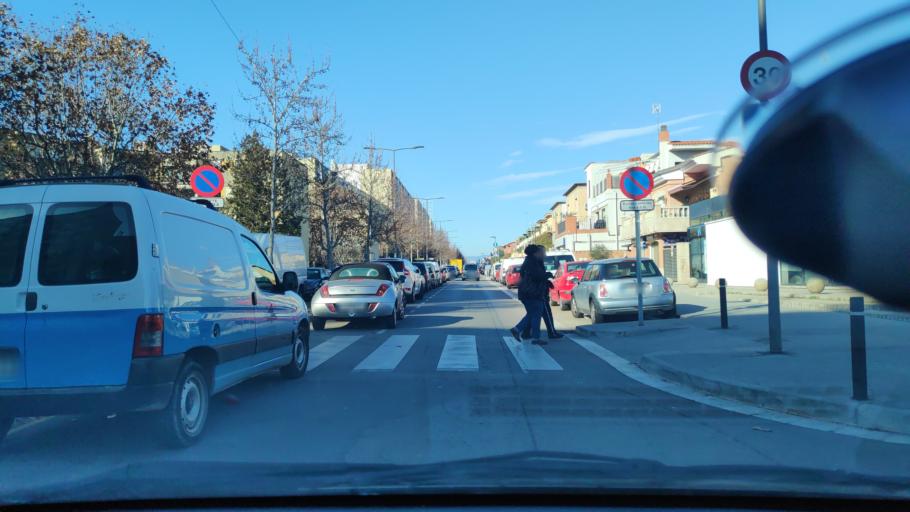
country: ES
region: Catalonia
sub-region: Provincia de Barcelona
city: Barbera del Valles
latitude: 41.5087
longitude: 2.1186
